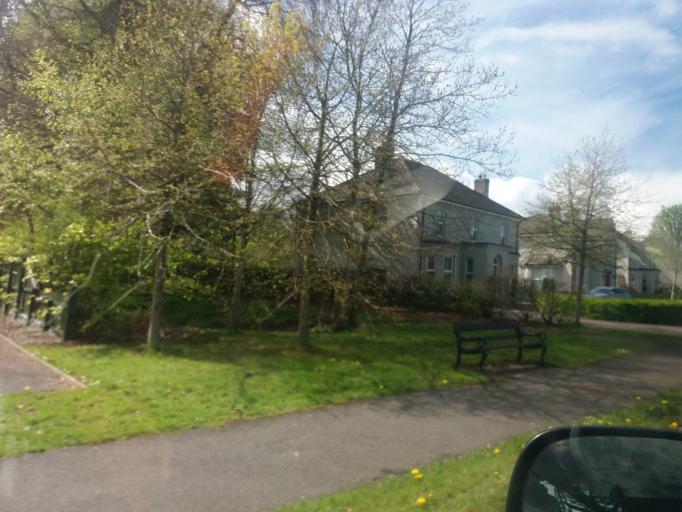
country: GB
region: Northern Ireland
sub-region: Fermanagh District
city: Enniskillen
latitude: 54.3601
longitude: -7.6731
